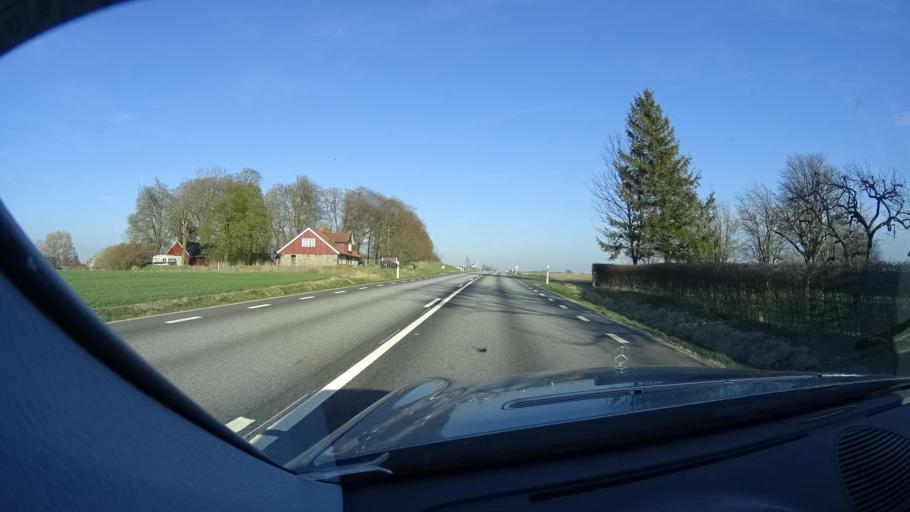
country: SE
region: Skane
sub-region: Eslovs Kommun
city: Eslov
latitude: 55.8597
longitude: 13.2547
